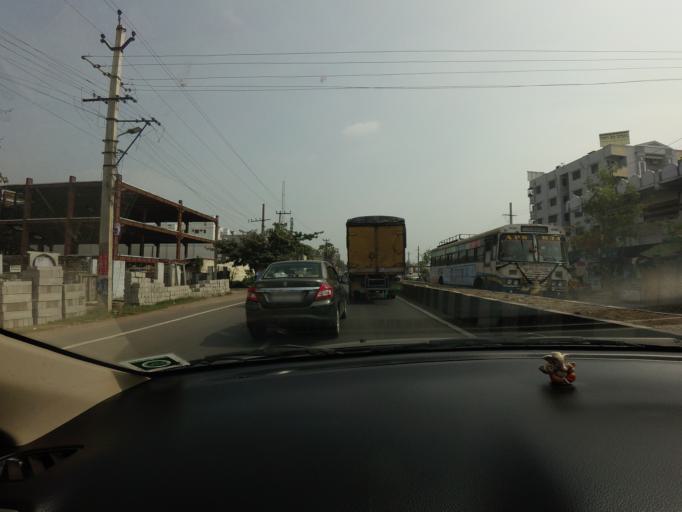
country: IN
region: Andhra Pradesh
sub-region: Krishna
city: Yanamalakuduru
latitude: 16.4868
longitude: 80.6793
